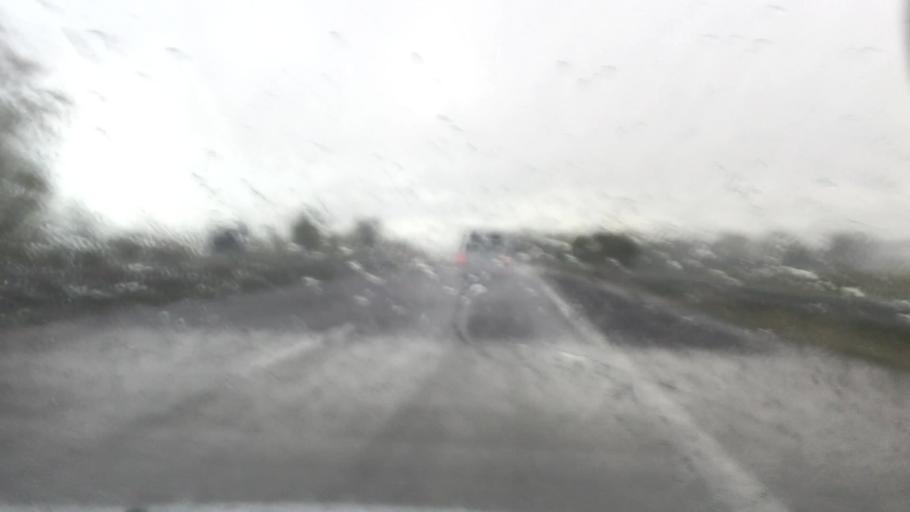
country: DE
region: Saxony-Anhalt
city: Biere
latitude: 51.9694
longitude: 11.6727
